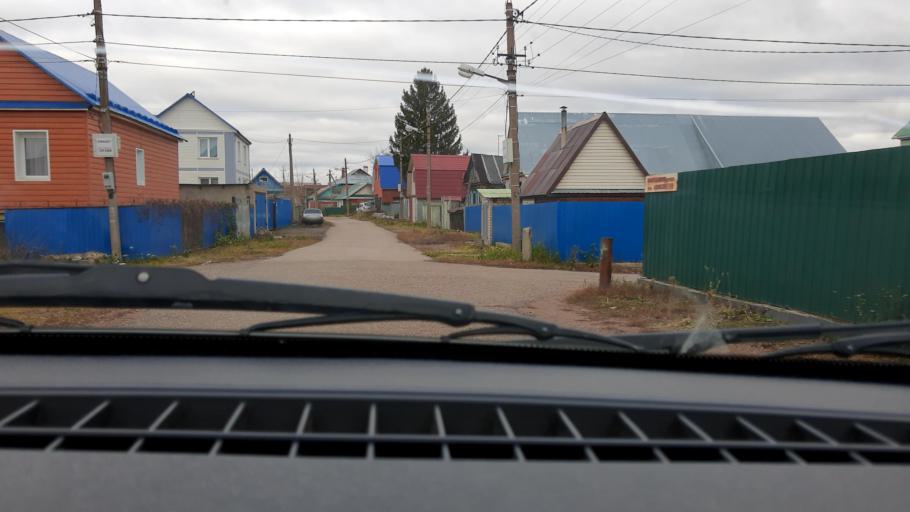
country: RU
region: Bashkortostan
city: Ufa
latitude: 54.7413
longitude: 55.9059
